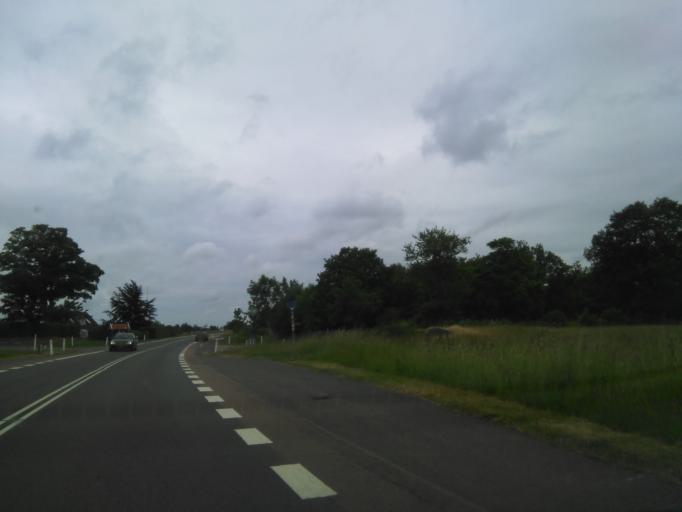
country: DK
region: Capital Region
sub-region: Bornholm Kommune
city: Akirkeby
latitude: 55.1109
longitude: 14.9119
